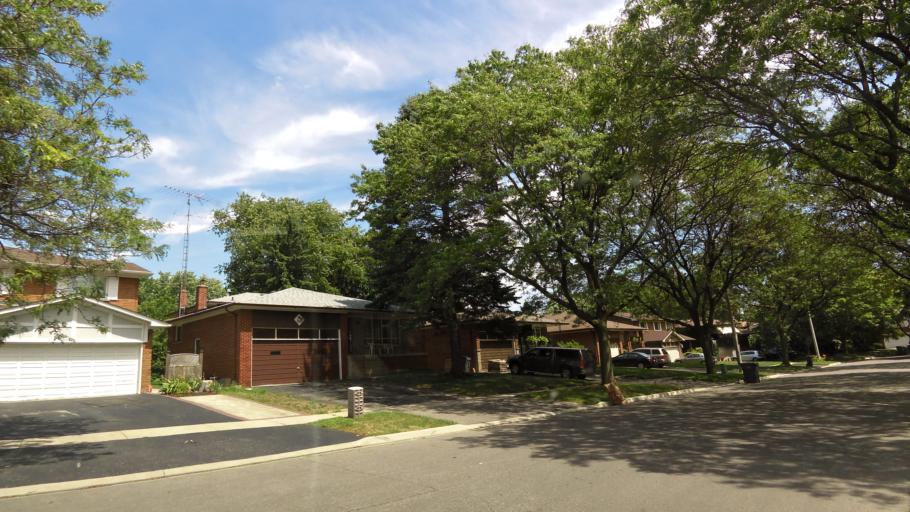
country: CA
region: Ontario
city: Etobicoke
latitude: 43.5872
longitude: -79.5632
